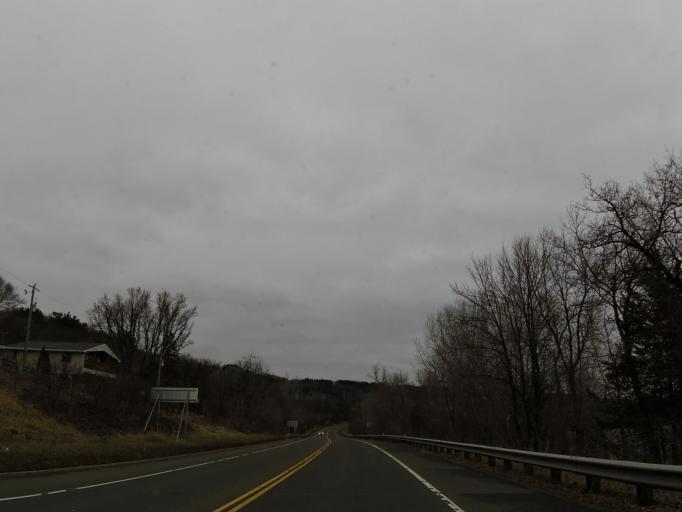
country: US
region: Minnesota
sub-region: Washington County
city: Stillwater
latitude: 45.0779
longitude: -92.8044
